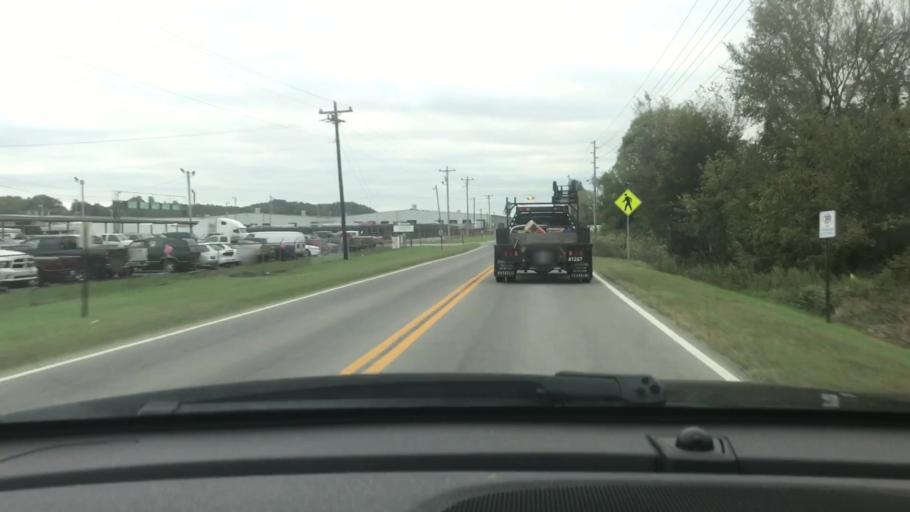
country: US
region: Tennessee
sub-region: Cheatham County
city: Ashland City
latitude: 36.2691
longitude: -87.0685
